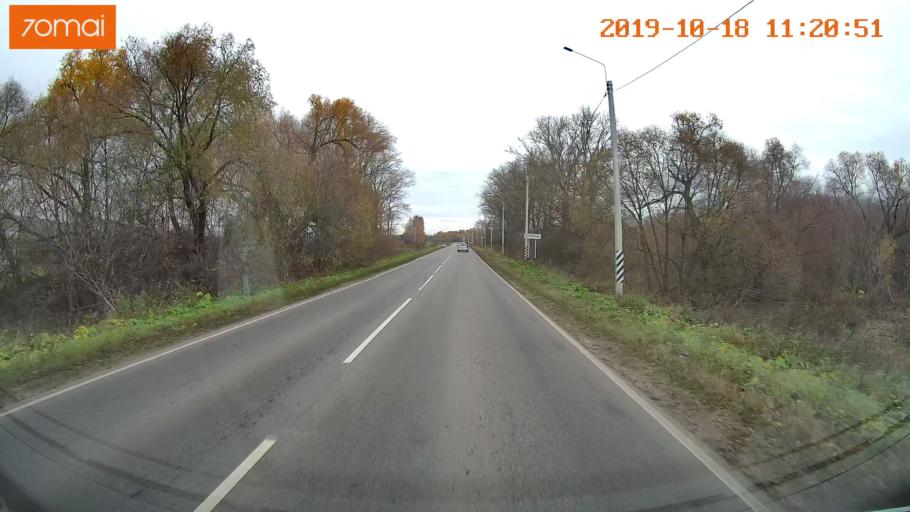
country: RU
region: Tula
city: Kimovsk
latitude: 54.0670
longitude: 38.5610
